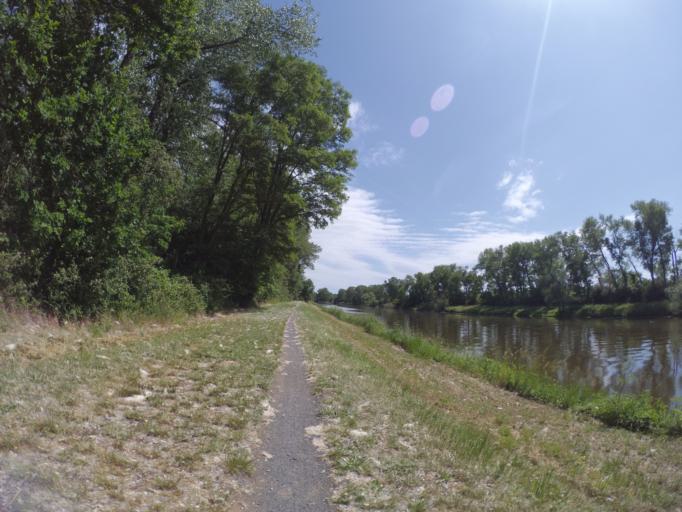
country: CZ
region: Central Bohemia
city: Milovice
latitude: 50.1703
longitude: 14.9045
